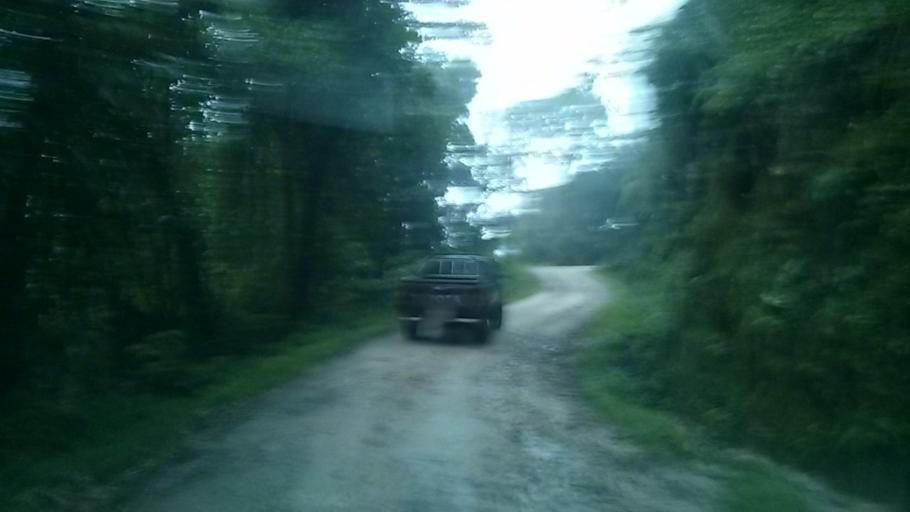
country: CR
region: San Jose
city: Ipis
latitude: 10.0222
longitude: -83.9433
